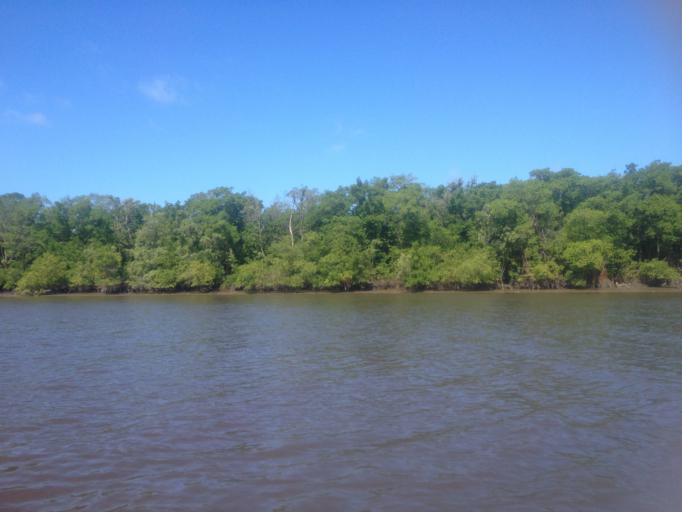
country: BR
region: Sergipe
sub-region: Indiaroba
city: Indiaroba
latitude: -11.4895
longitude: -37.4008
